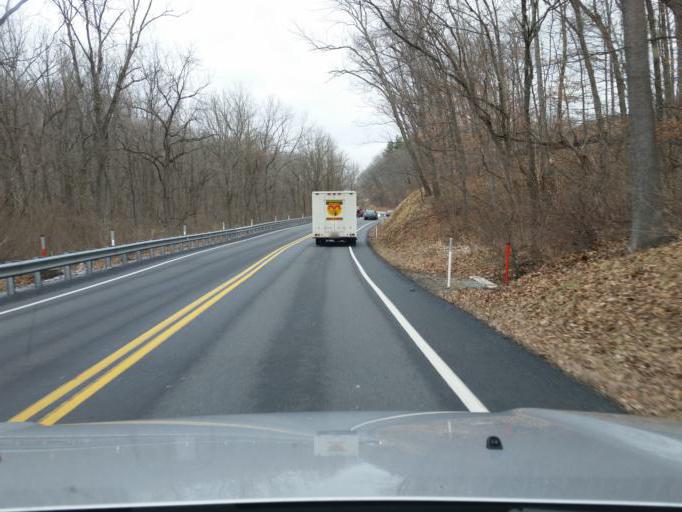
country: US
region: Pennsylvania
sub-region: Dauphin County
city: Rutherford
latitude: 40.2912
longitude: -76.7642
